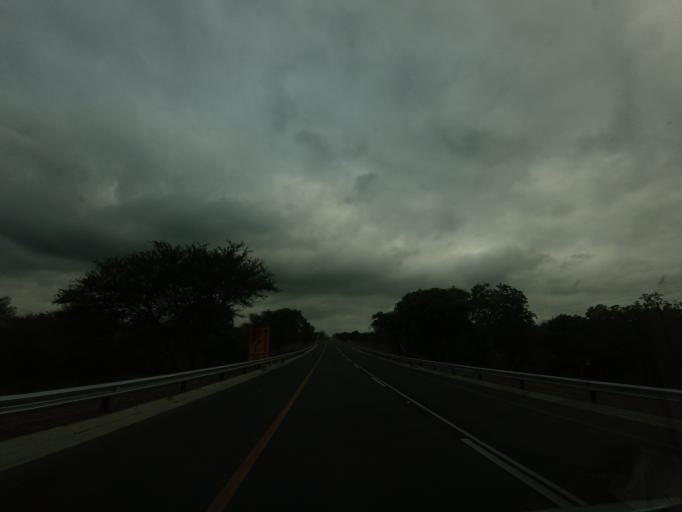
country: ZA
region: Mpumalanga
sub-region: Ehlanzeni District
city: Komatipoort
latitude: -25.4406
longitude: 31.7412
